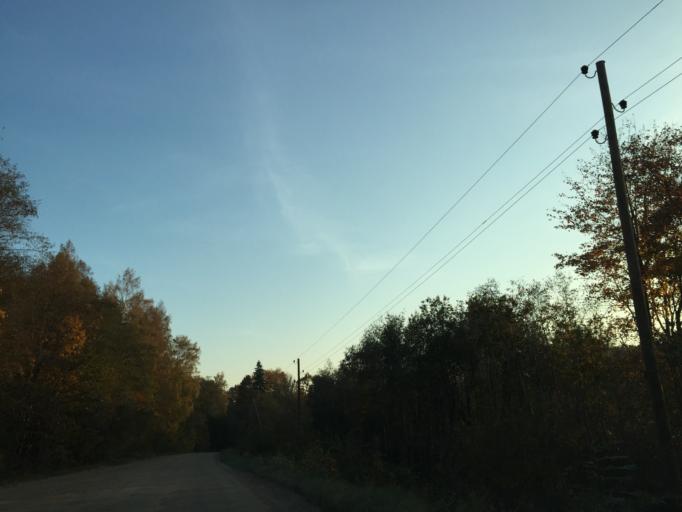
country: LV
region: Vainode
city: Vainode
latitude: 56.5055
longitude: 21.8242
